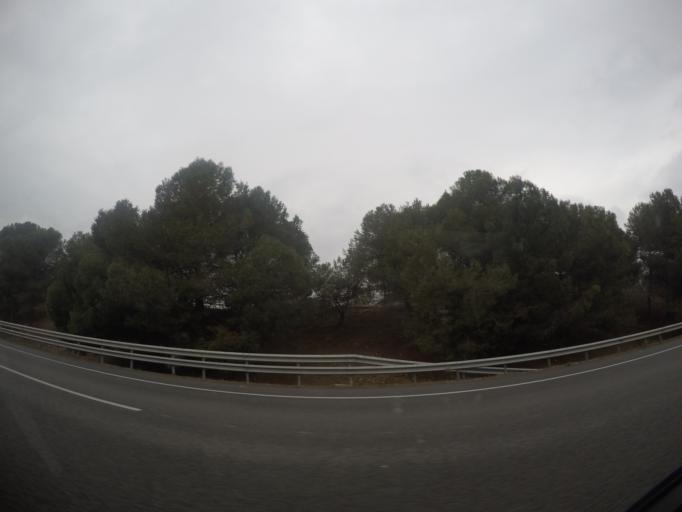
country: ES
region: Catalonia
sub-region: Provincia de Tarragona
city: Sant Jaume dels Domenys
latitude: 41.2938
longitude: 1.5984
